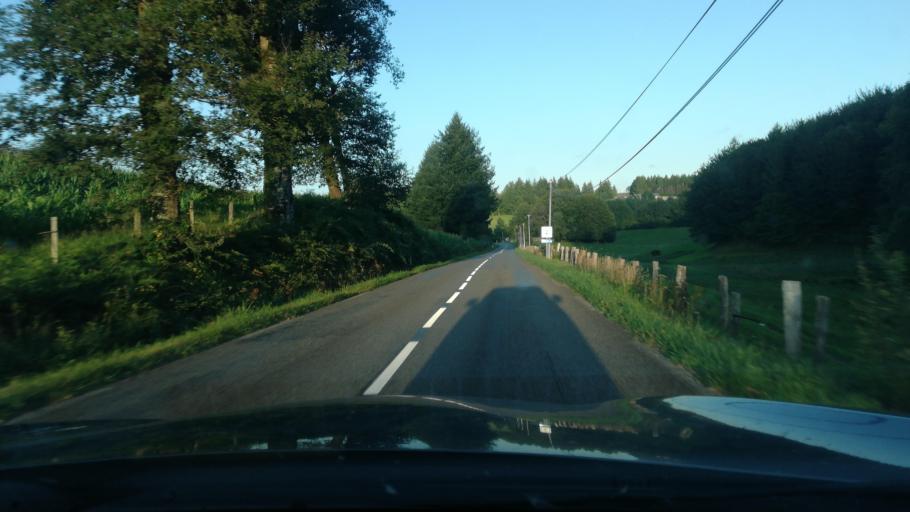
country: FR
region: Midi-Pyrenees
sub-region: Departement du Lot
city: Saint-Cere
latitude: 44.8795
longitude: 2.0118
